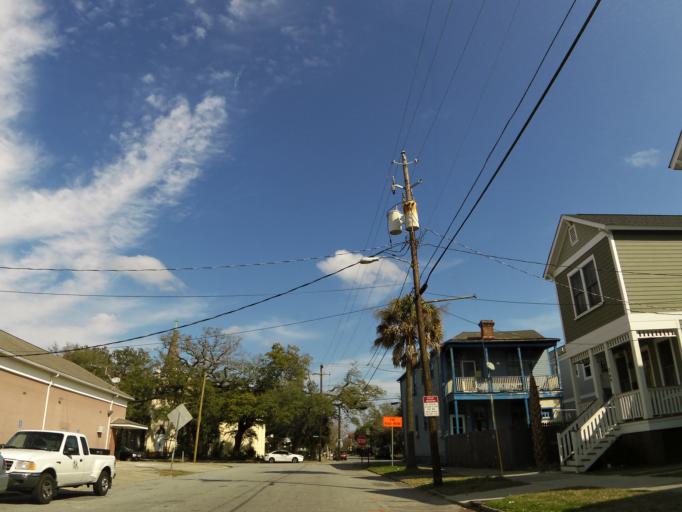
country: US
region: South Carolina
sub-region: Charleston County
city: Charleston
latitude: 32.7957
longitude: -79.9505
